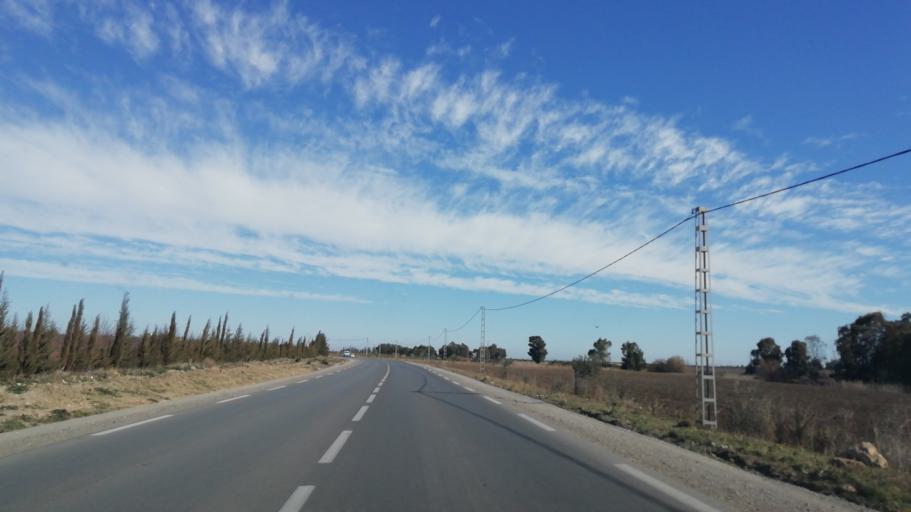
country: DZ
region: Sidi Bel Abbes
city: Sidi Bel Abbes
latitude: 35.0525
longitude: -0.8256
